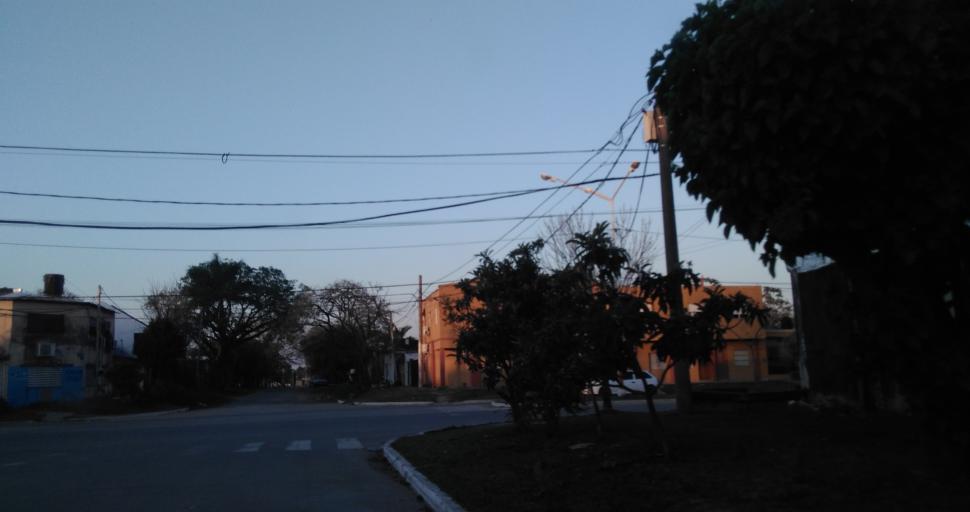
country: AR
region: Chaco
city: Resistencia
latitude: -27.4555
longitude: -58.9735
